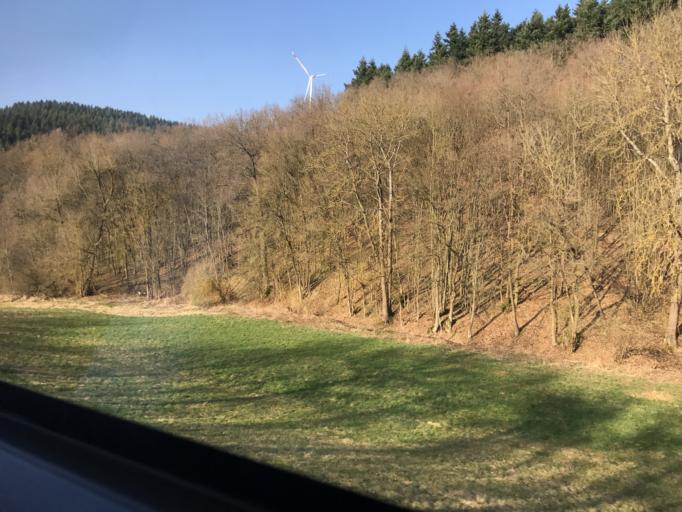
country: DE
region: Rheinland-Pfalz
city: Callbach
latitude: 49.7005
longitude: 7.7149
